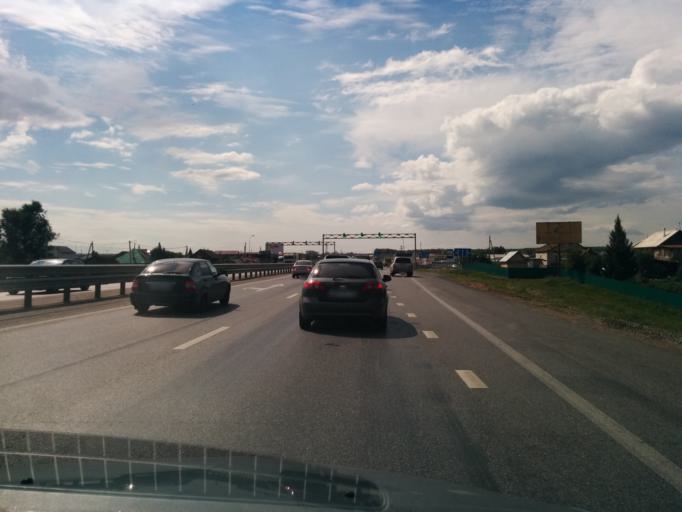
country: RU
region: Bashkortostan
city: Avdon
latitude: 54.5027
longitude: 55.9025
